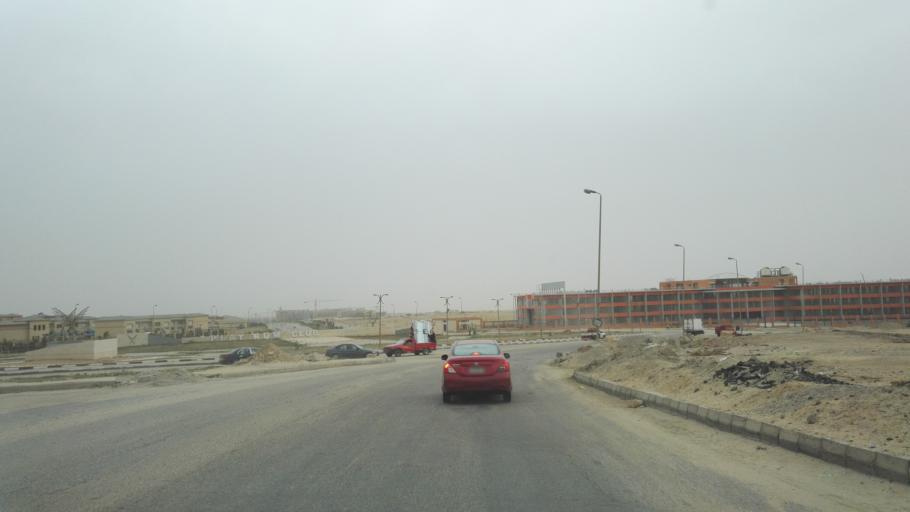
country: EG
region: Muhafazat al Qalyubiyah
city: Al Khankah
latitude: 30.0412
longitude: 31.5246
